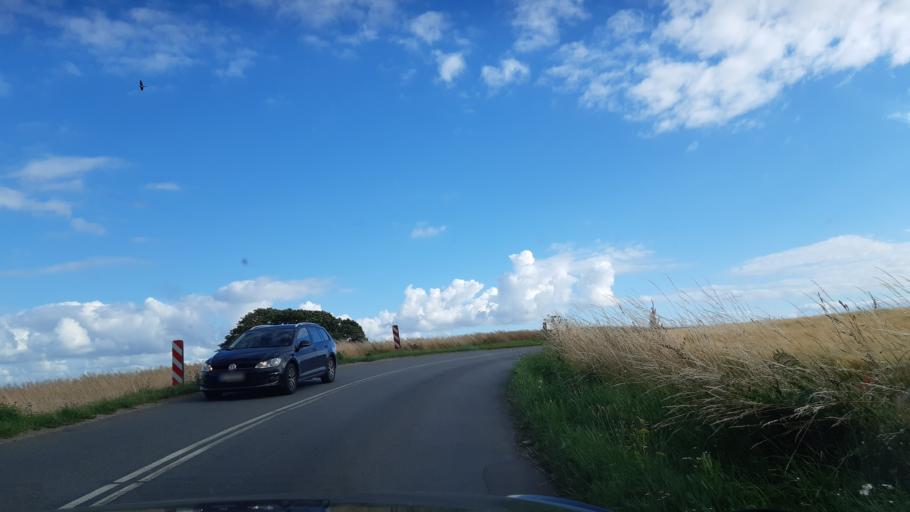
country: DK
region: Zealand
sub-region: Odsherred Kommune
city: Horve
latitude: 55.8118
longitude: 11.4318
